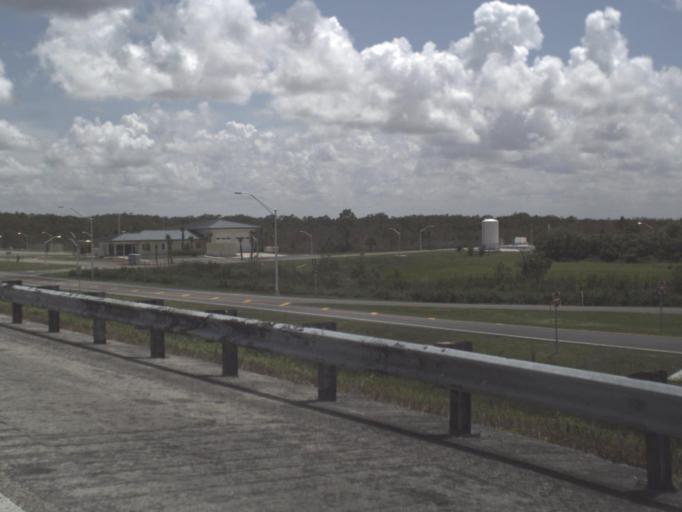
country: US
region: Florida
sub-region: Collier County
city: Immokalee
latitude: 26.1683
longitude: -81.0772
